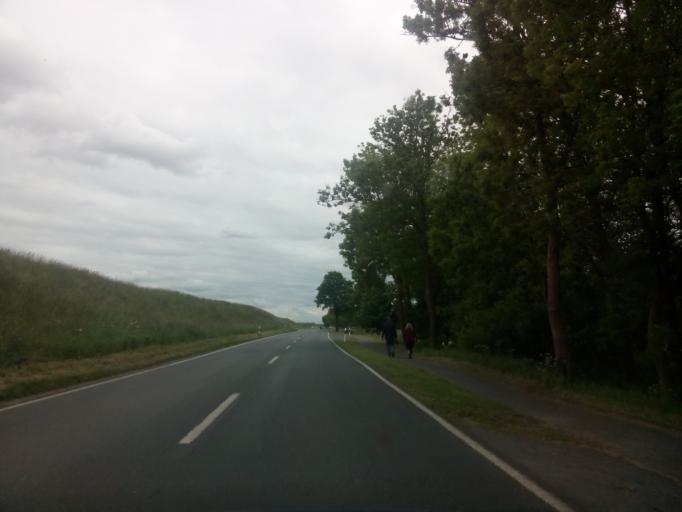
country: DE
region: Lower Saxony
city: Lemwerder
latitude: 53.1218
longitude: 8.6376
